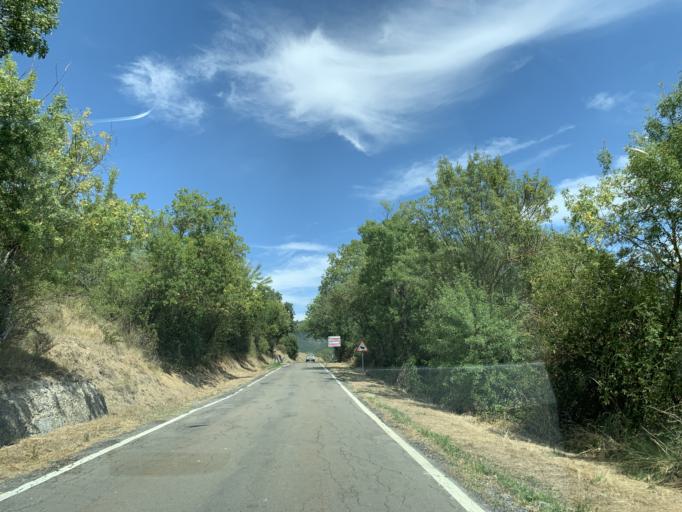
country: ES
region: Aragon
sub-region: Provincia de Huesca
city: Borau
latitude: 42.5941
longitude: -0.6313
